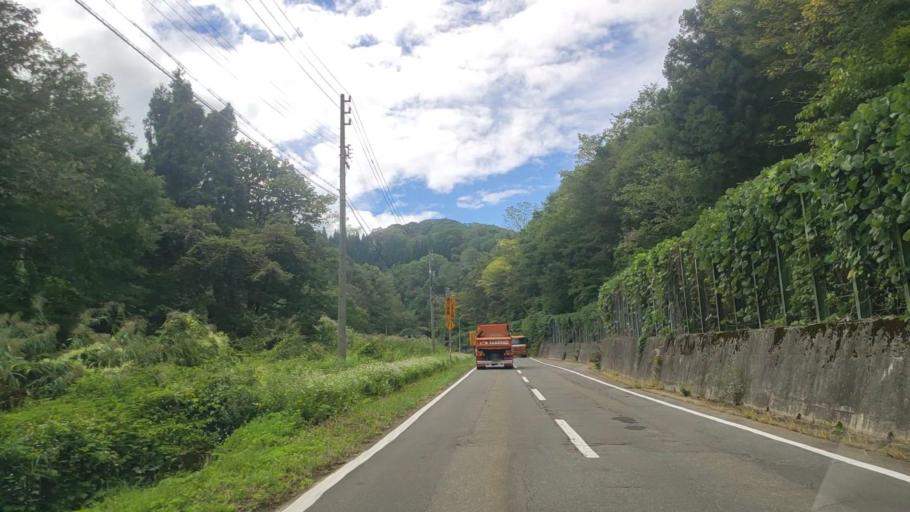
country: JP
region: Nagano
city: Iiyama
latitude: 36.8801
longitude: 138.3200
